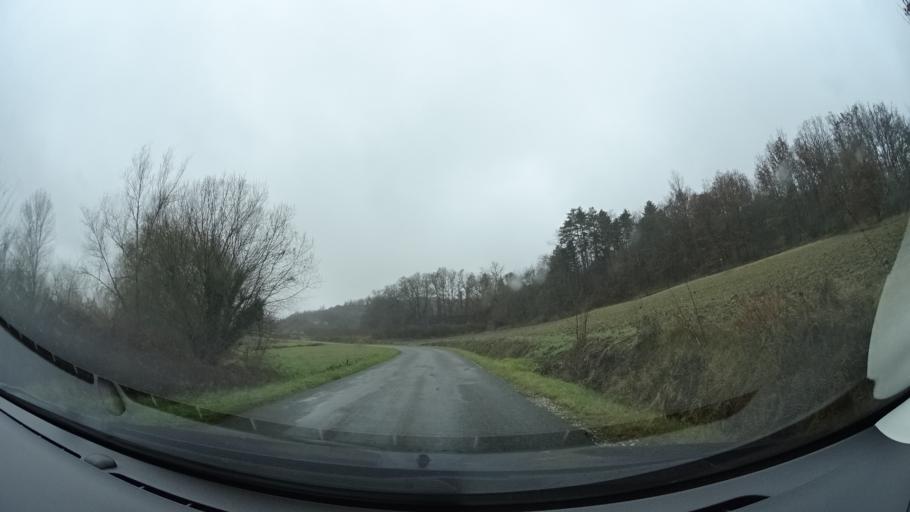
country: FR
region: Midi-Pyrenees
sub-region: Departement du Lot
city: Montcuq
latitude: 44.3616
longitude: 1.2301
